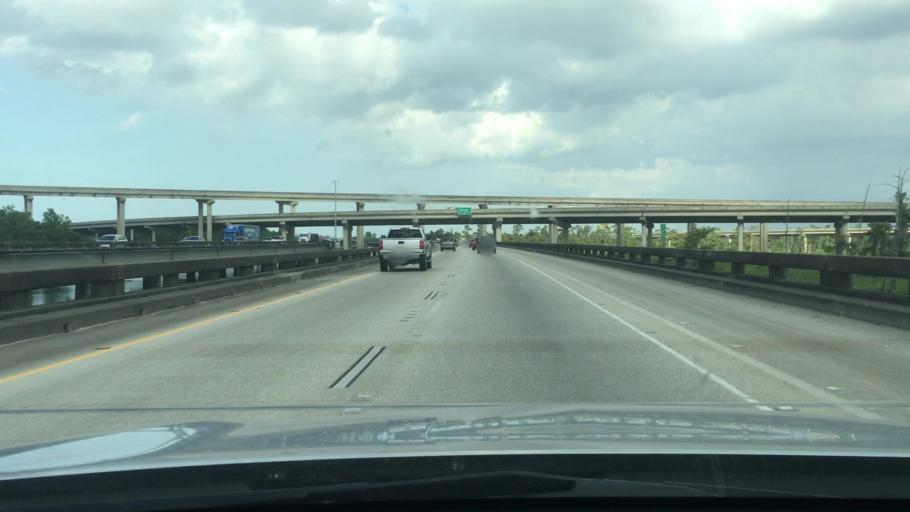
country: US
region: Louisiana
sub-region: Jefferson Parish
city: Kenner
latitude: 30.0069
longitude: -90.2949
